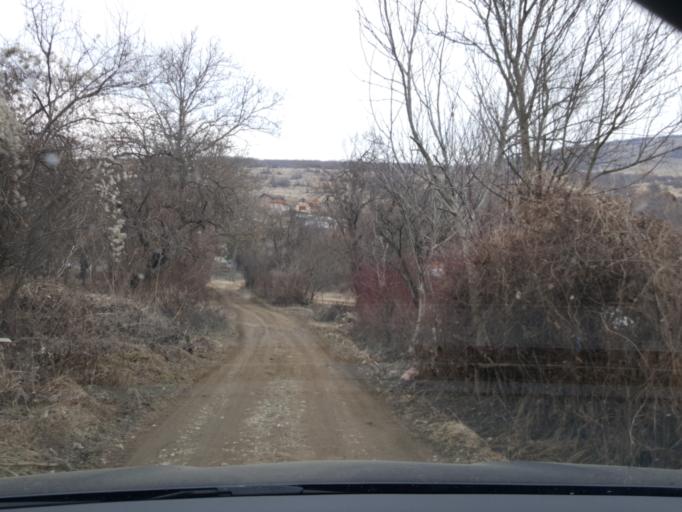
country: RS
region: Central Serbia
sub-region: Pirotski Okrug
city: Dimitrovgrad
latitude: 43.0002
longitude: 22.7633
